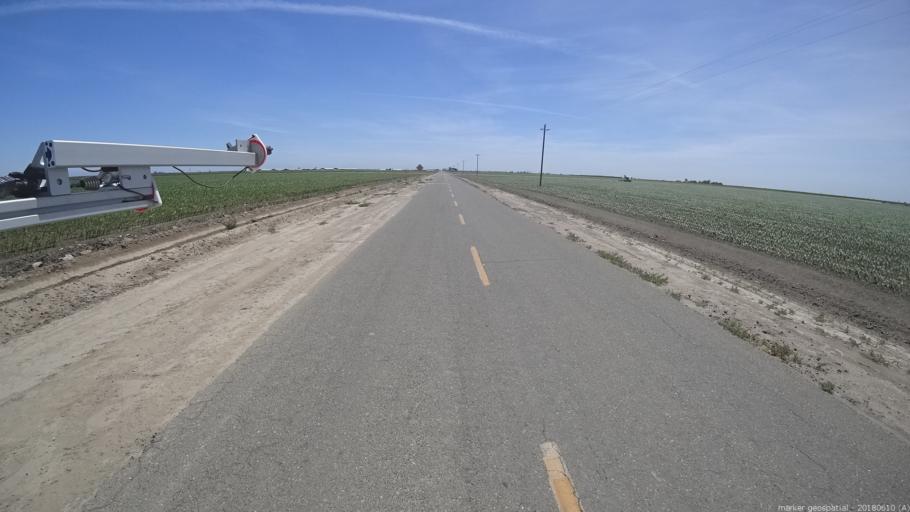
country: US
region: California
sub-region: Merced County
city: Dos Palos
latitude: 37.0546
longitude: -120.4715
